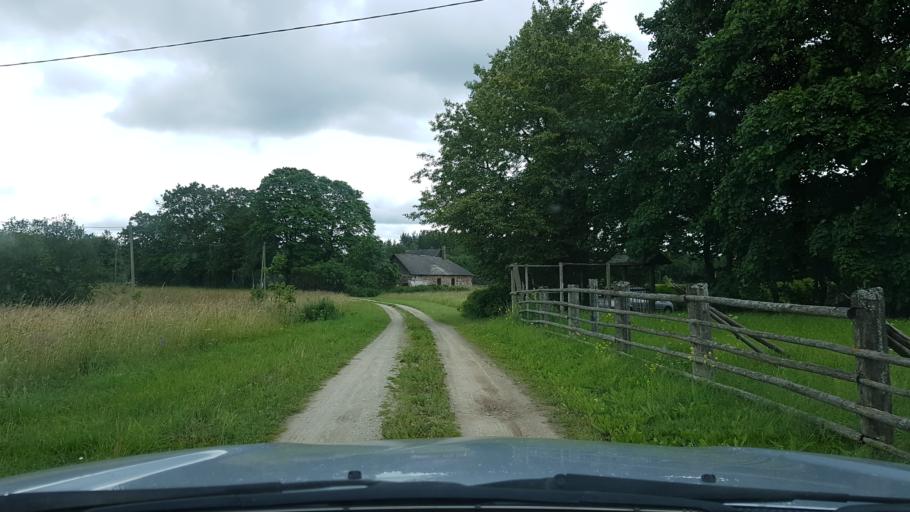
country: EE
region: Ida-Virumaa
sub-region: Sillamaee linn
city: Sillamae
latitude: 59.3690
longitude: 27.7496
